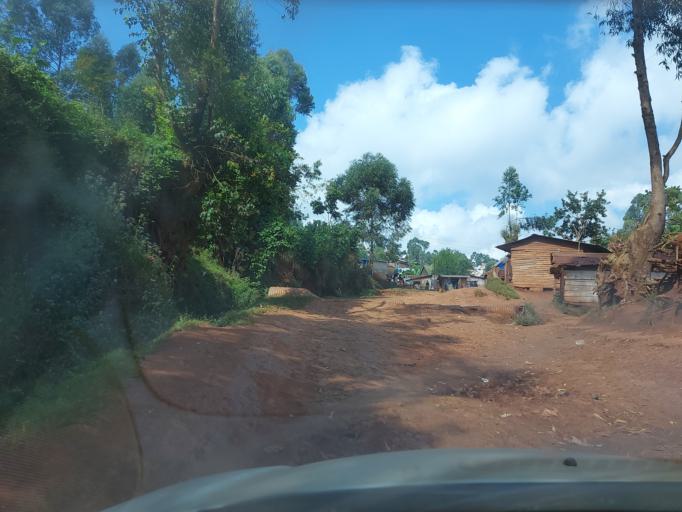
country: CD
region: South Kivu
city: Bukavu
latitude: -2.5142
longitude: 28.8392
